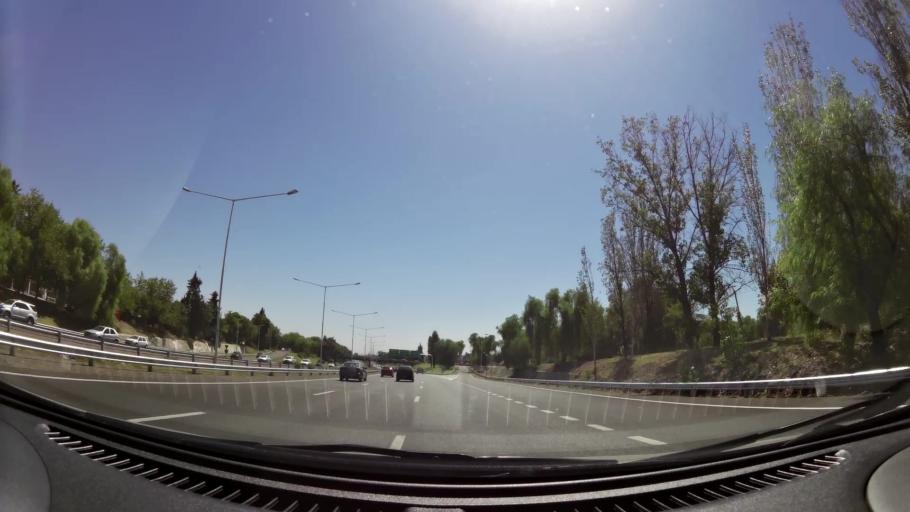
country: AR
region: Mendoza
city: Mendoza
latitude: -32.9073
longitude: -68.8203
